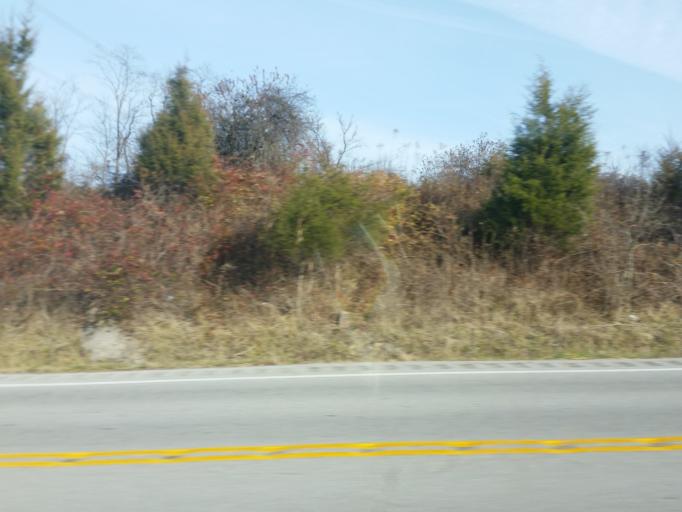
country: US
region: Kentucky
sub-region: Pendleton County
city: Falmouth
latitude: 38.5674
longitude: -84.2926
